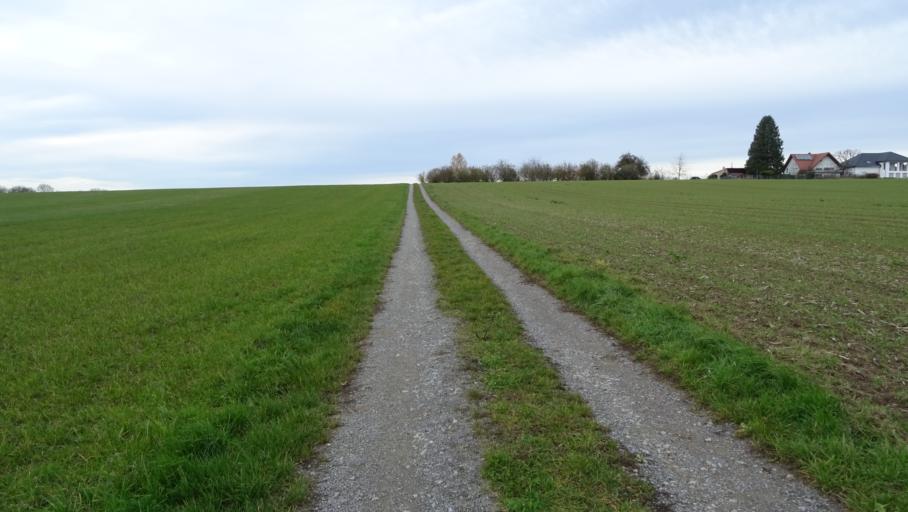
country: DE
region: Baden-Wuerttemberg
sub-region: Karlsruhe Region
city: Mosbach
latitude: 49.3395
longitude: 9.1511
